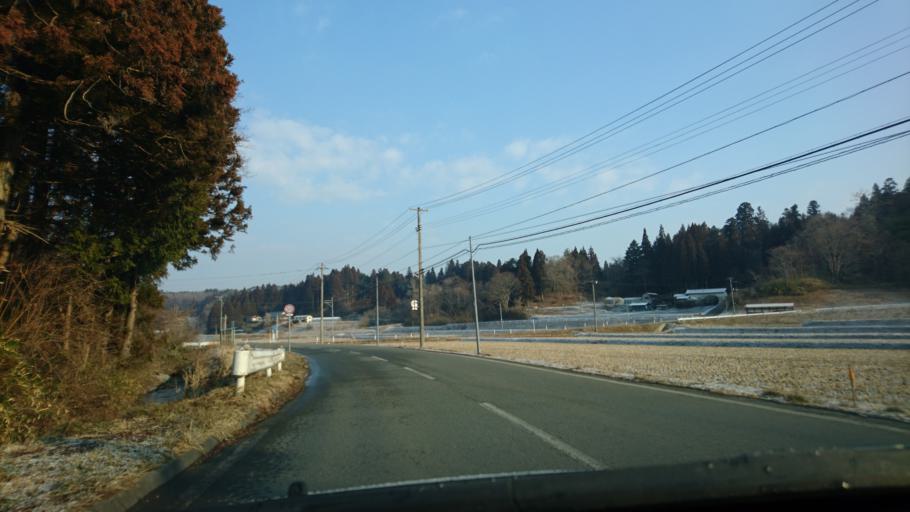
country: JP
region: Iwate
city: Ichinoseki
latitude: 38.9273
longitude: 141.3863
